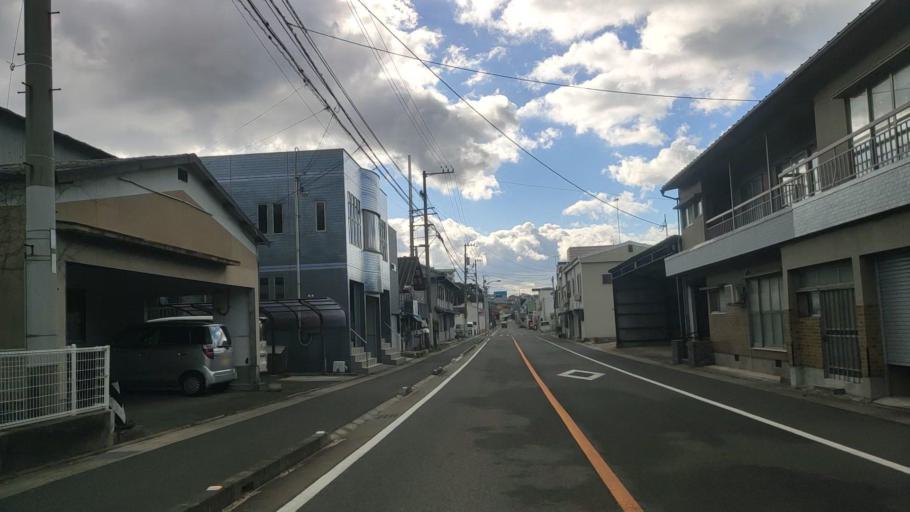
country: JP
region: Ehime
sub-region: Shikoku-chuo Shi
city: Matsuyama
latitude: 33.8843
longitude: 132.7016
